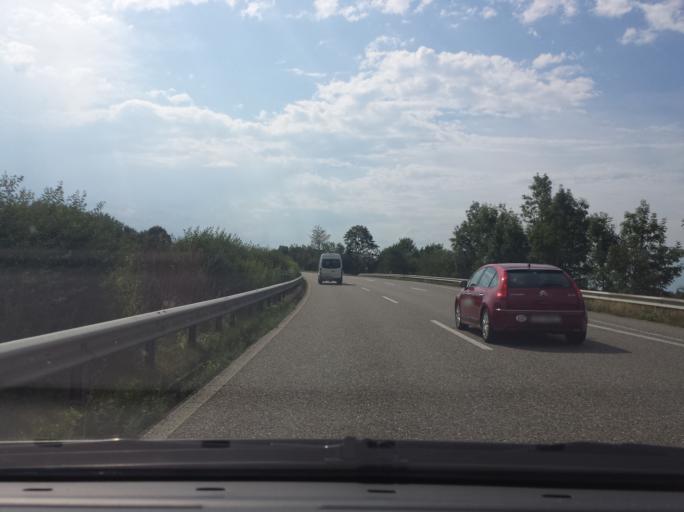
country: CH
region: Saint Gallen
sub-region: Wahlkreis Rheintal
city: Rheineck
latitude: 47.4804
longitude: 9.5795
